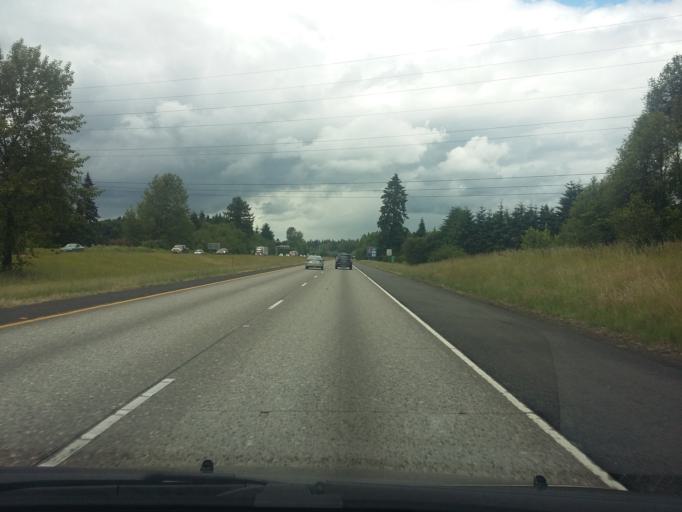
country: US
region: Washington
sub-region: Clark County
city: Five Corners
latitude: 45.6700
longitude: -122.5808
